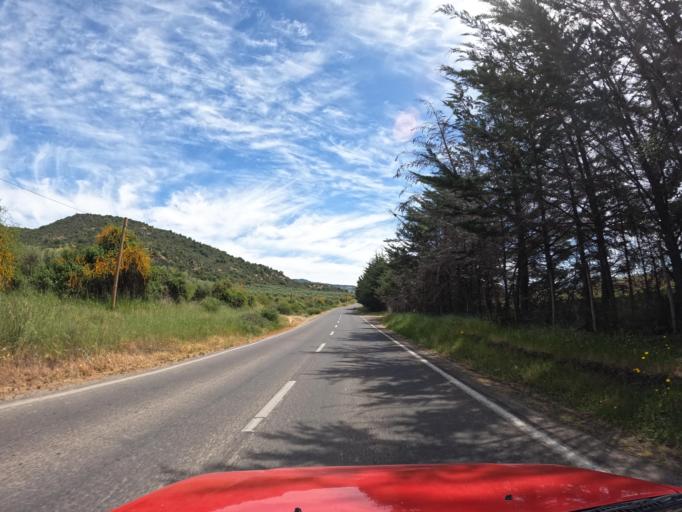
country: CL
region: Maule
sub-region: Provincia de Talca
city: Talca
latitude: -35.1211
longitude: -71.6510
